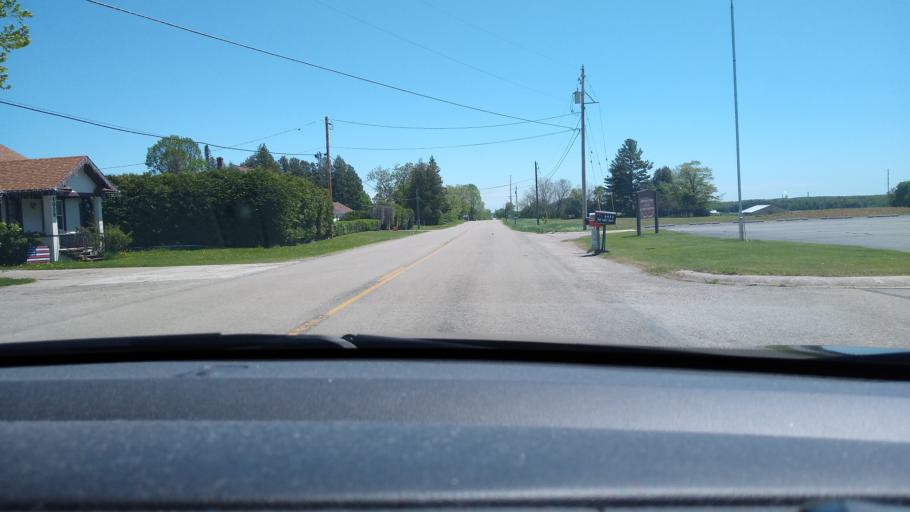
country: US
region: Michigan
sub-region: Delta County
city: Escanaba
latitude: 45.8261
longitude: -87.1668
